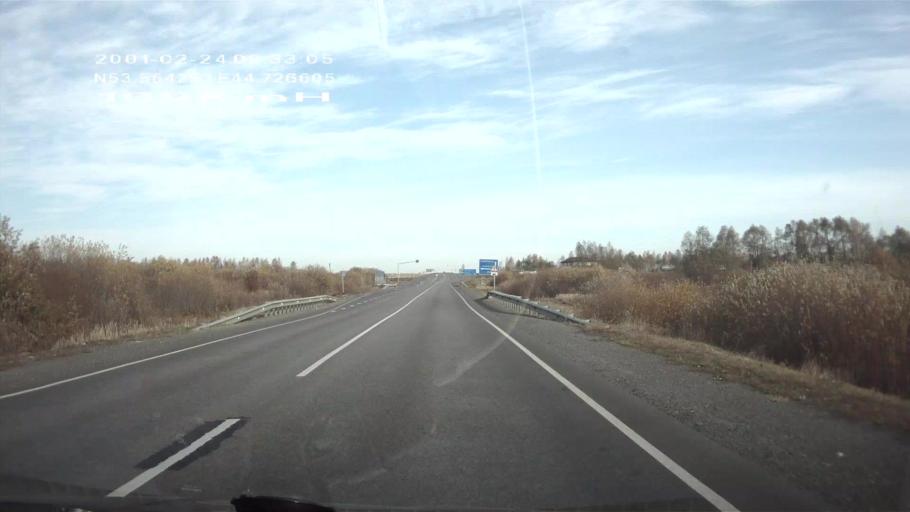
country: RU
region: Penza
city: Mokshan
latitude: 53.5648
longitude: 44.7266
